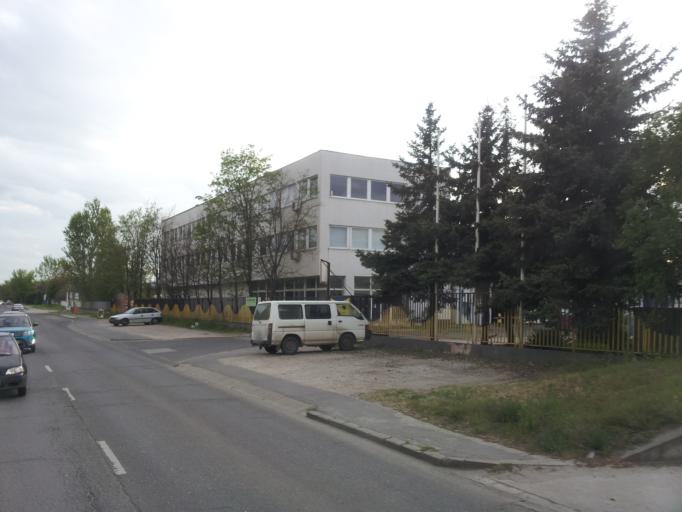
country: HU
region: Budapest
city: Budapest XV. keruelet
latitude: 47.5844
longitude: 19.1311
